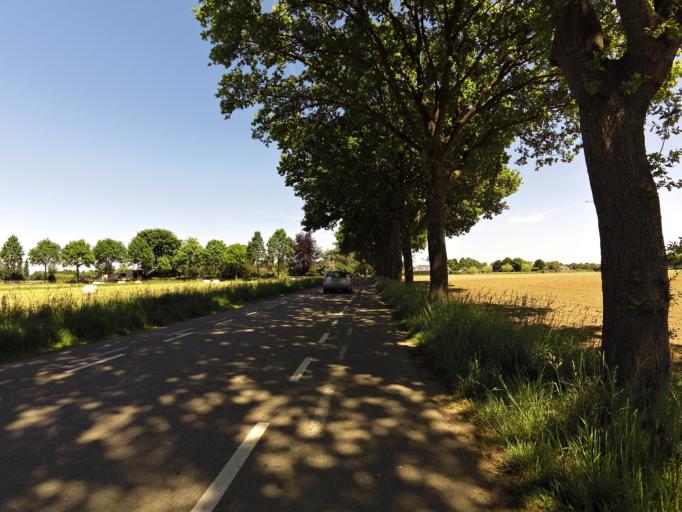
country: NL
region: Gelderland
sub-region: Gemeente Doesburg
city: Doesburg
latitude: 52.0270
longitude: 6.1915
